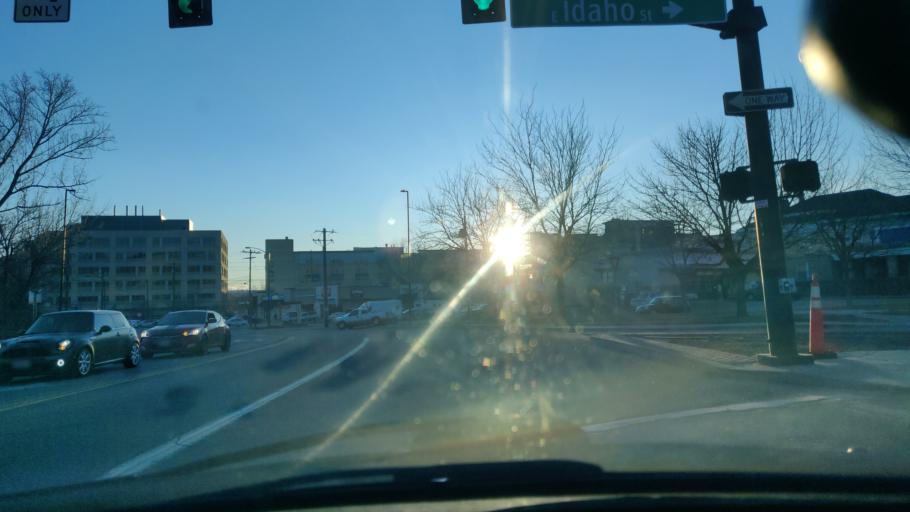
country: US
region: Idaho
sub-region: Ada County
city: Boise
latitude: 43.6111
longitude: -116.1931
